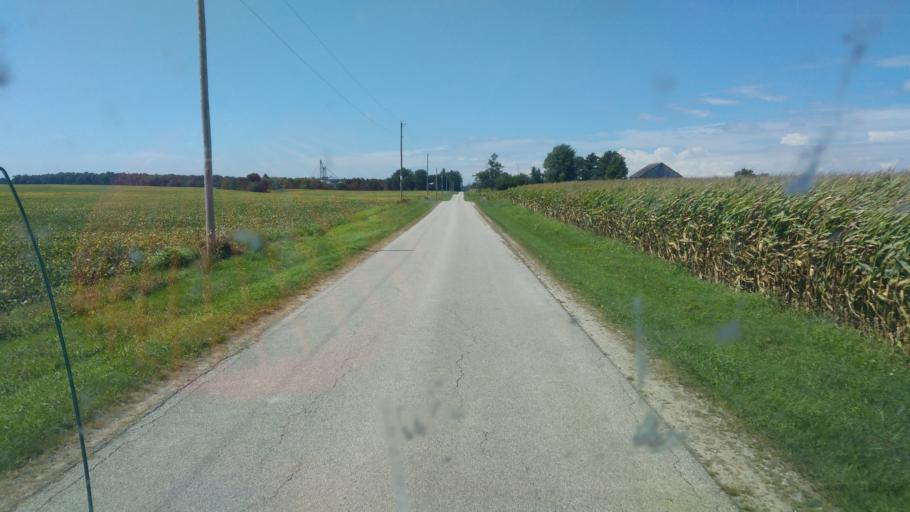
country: US
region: Ohio
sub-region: Crawford County
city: Bucyrus
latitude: 40.7899
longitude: -83.1020
